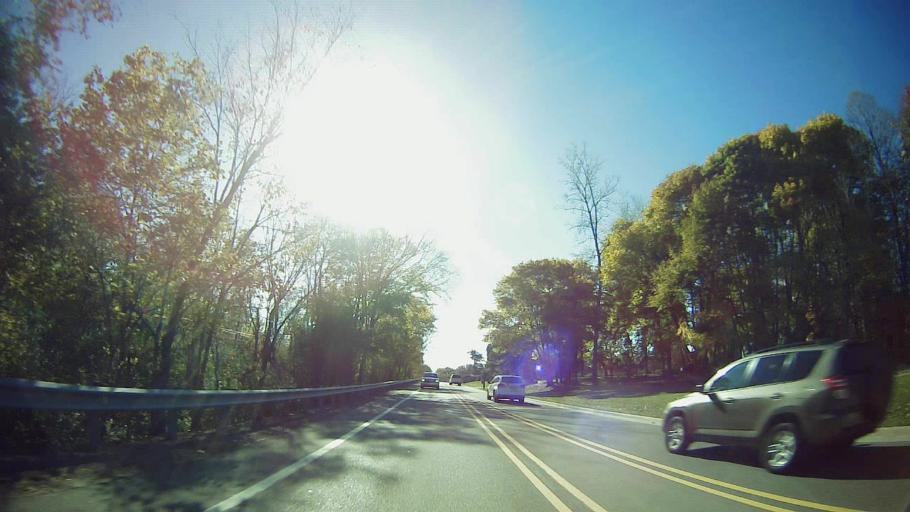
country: US
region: Michigan
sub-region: Oakland County
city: Farmington Hills
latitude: 42.4917
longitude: -83.3779
